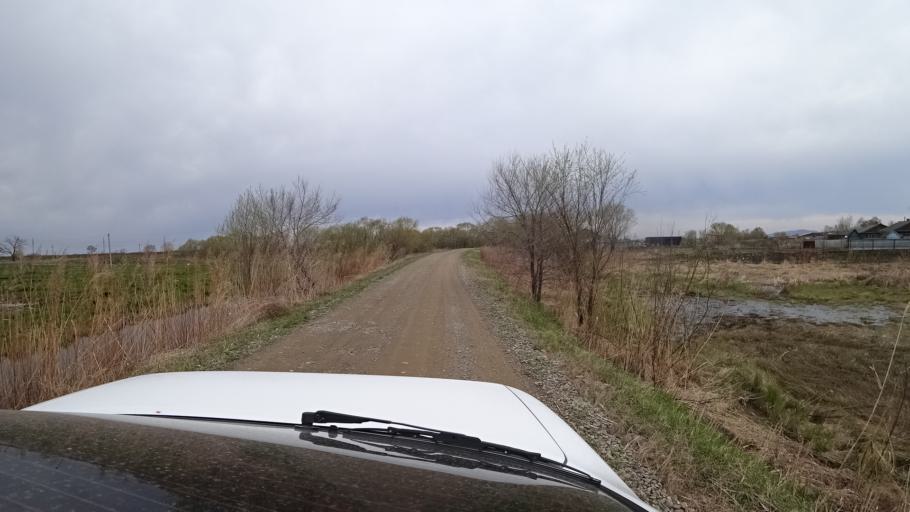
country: RU
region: Primorskiy
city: Dal'nerechensk
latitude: 45.9752
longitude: 133.7518
